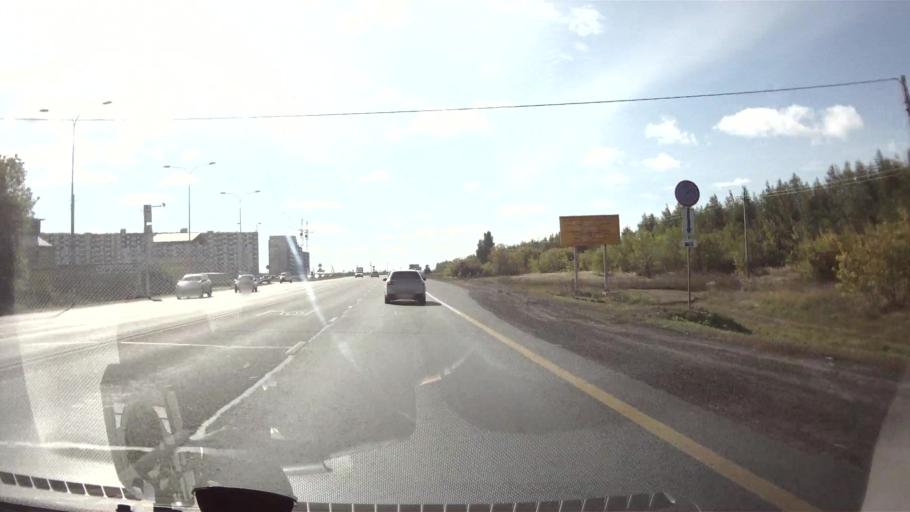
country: RU
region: Ulyanovsk
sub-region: Ulyanovskiy Rayon
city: Ulyanovsk
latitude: 54.2869
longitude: 48.2563
